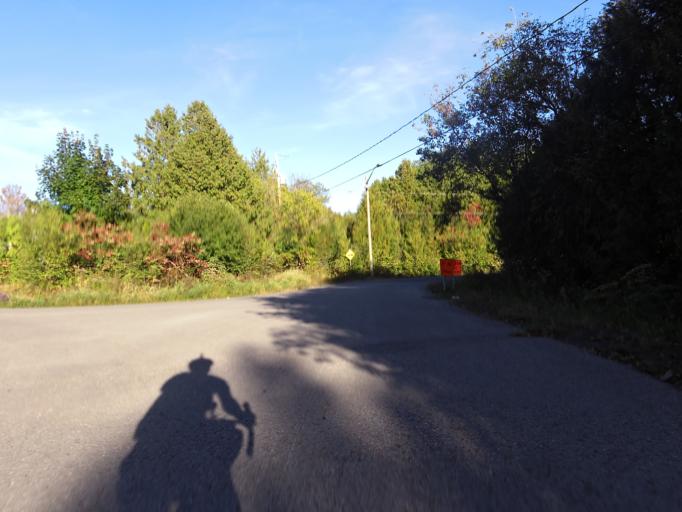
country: CA
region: Ontario
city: Bells Corners
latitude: 45.4279
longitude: -75.8769
